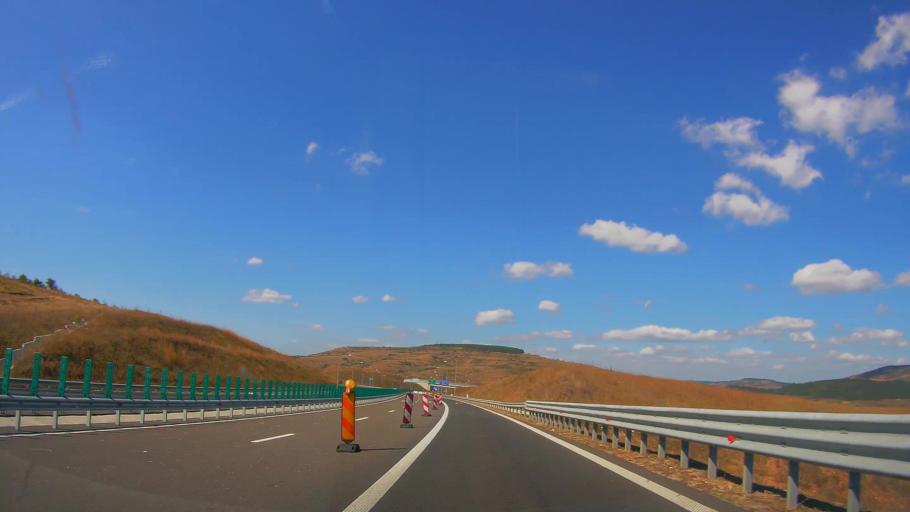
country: RO
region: Cluj
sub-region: Comuna Baciu
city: Mera
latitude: 46.8064
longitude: 23.4248
